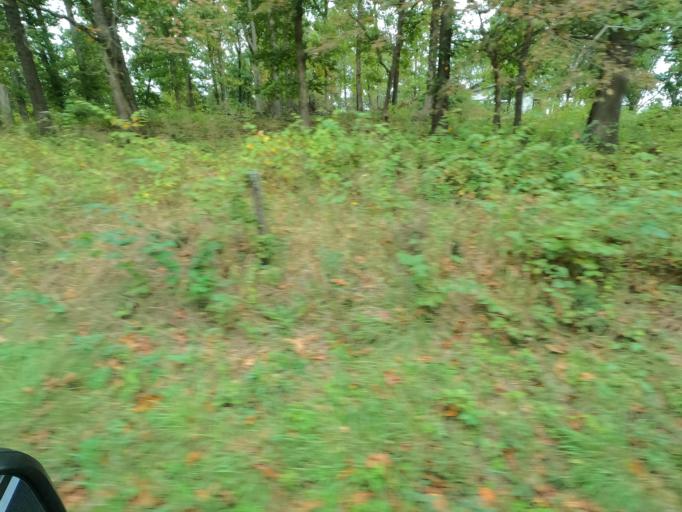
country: US
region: Tennessee
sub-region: Washington County
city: Jonesborough
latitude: 36.2237
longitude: -82.5847
